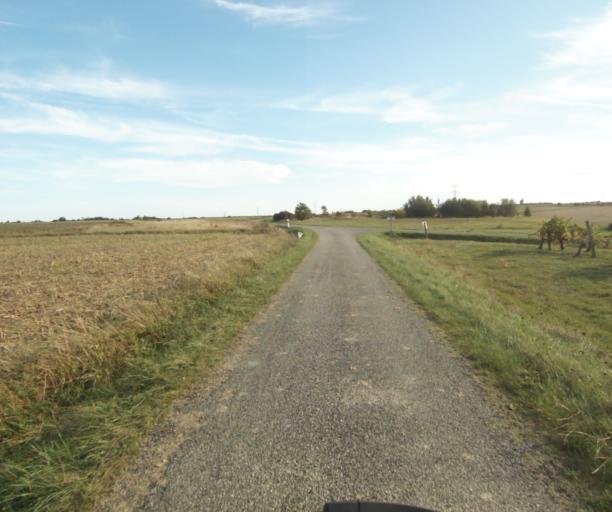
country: FR
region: Midi-Pyrenees
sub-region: Departement du Tarn-et-Garonne
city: Finhan
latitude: 43.9114
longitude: 1.1137
